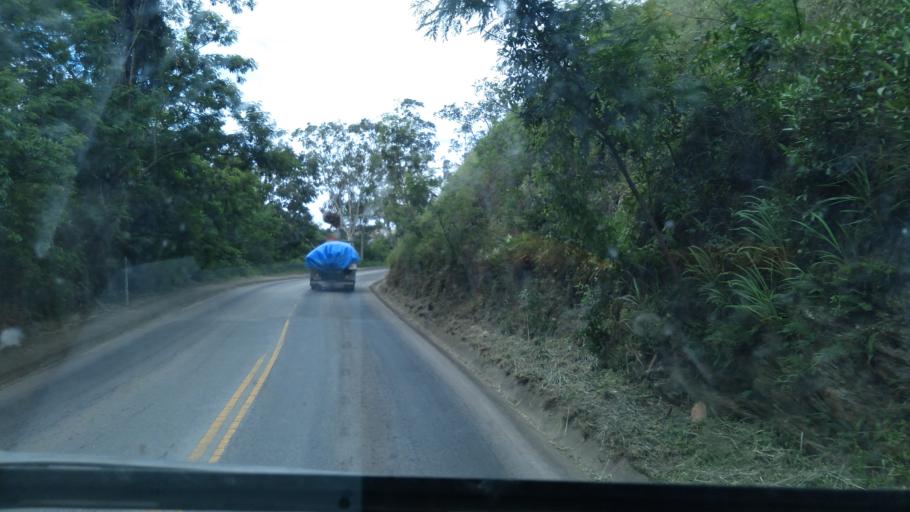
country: BR
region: Minas Gerais
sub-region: Belo Horizonte
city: Belo Horizonte
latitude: -19.8750
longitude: -43.8582
